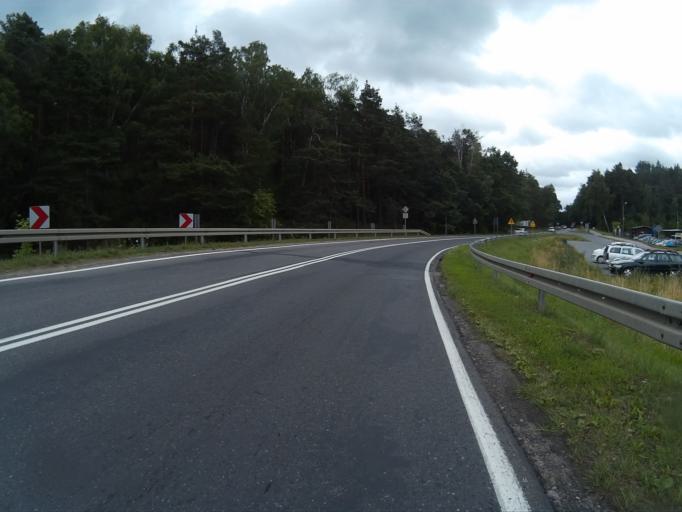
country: PL
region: Kujawsko-Pomorskie
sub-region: Powiat tucholski
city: Tuchola
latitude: 53.5631
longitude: 17.9007
